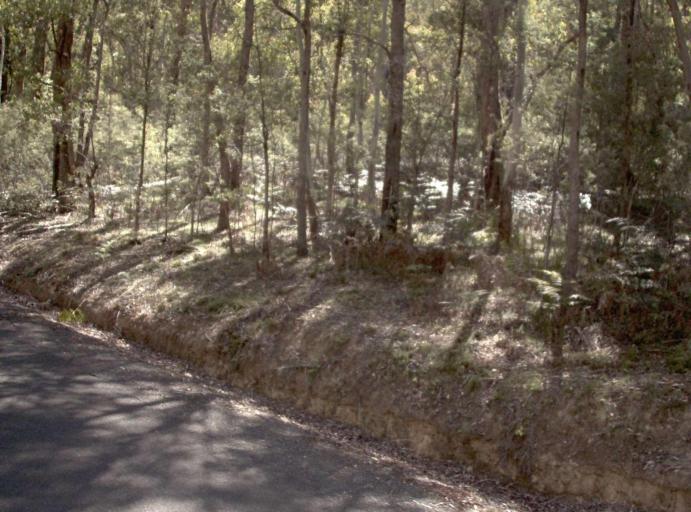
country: AU
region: New South Wales
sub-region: Bombala
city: Bombala
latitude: -37.1200
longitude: 148.7521
